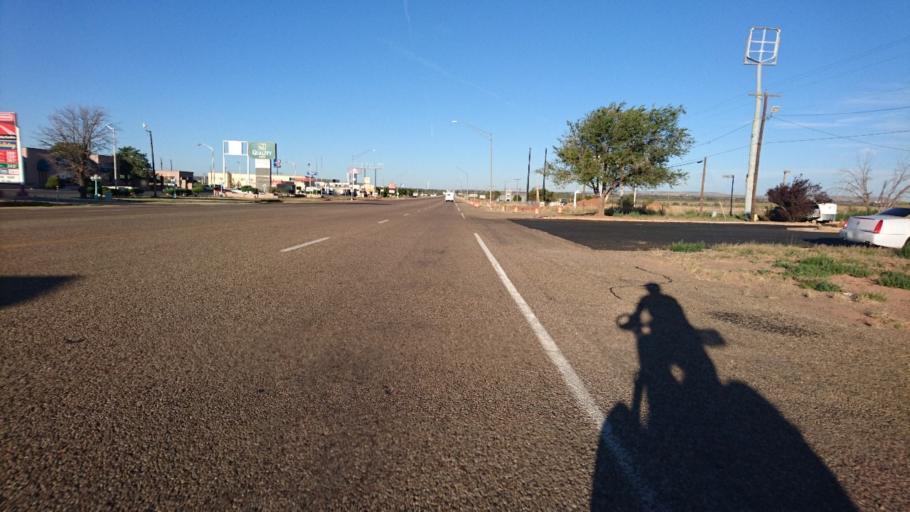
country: US
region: New Mexico
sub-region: Quay County
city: Tucumcari
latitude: 35.1720
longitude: -103.6800
